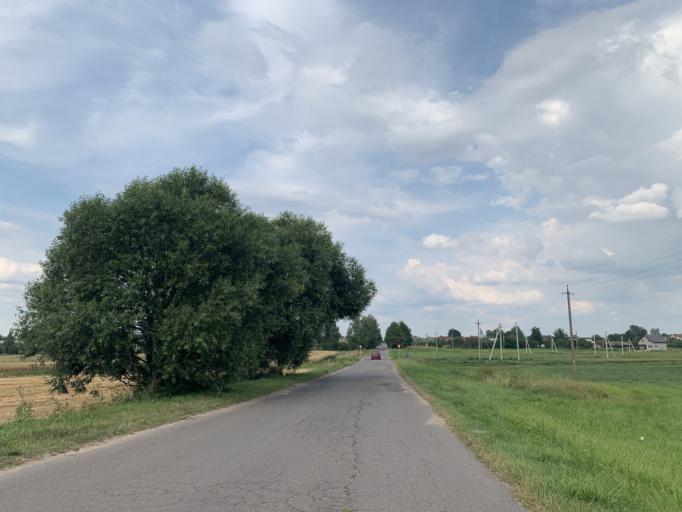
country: BY
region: Minsk
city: Nyasvizh
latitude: 53.2040
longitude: 26.6795
